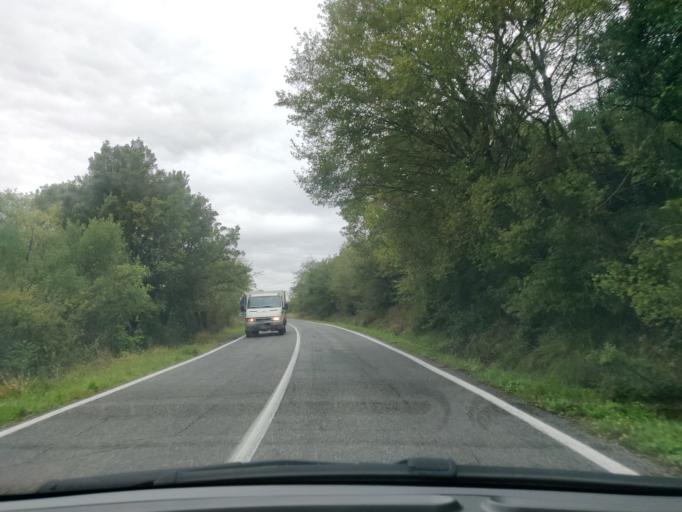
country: IT
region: Latium
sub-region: Citta metropolitana di Roma Capitale
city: Allumiere
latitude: 42.1461
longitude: 11.8965
